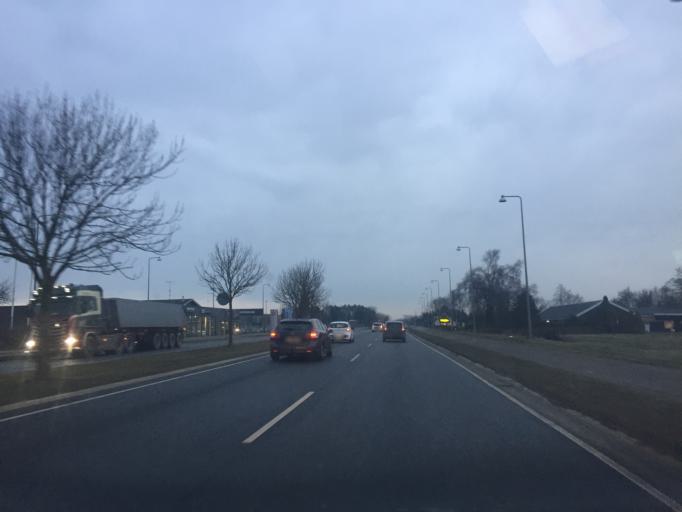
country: DK
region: Zealand
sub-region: Solrod Kommune
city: Solrod
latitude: 55.5029
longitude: 12.1984
